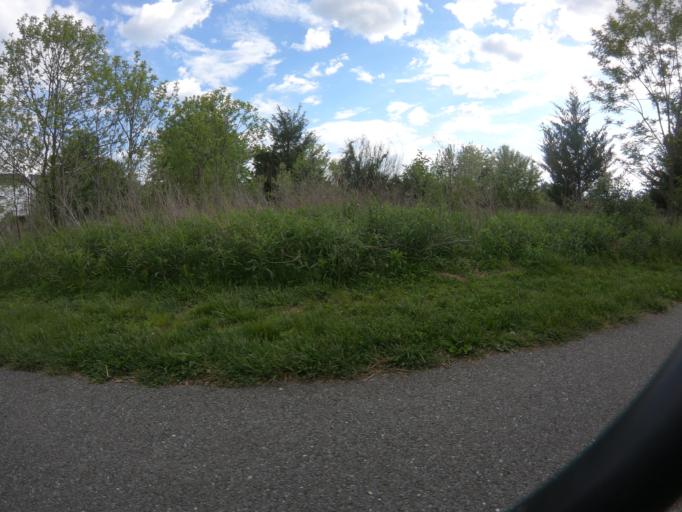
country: US
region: Maryland
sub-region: Montgomery County
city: Clarksburg
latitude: 39.2092
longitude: -77.2551
